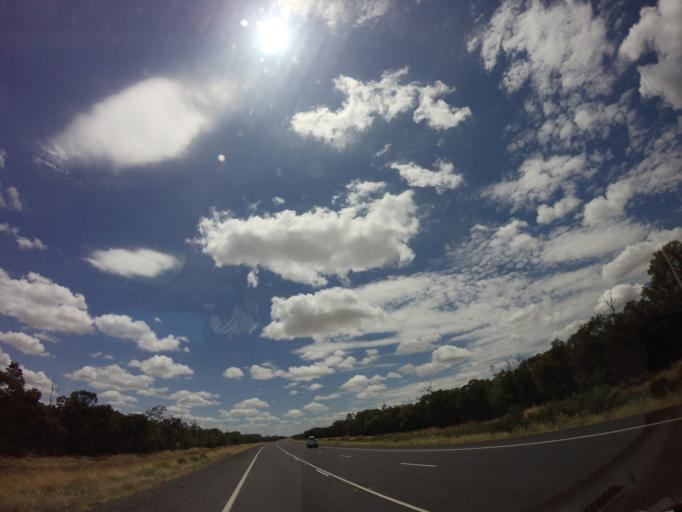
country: AU
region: New South Wales
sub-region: Moree Plains
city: Boggabilla
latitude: -28.8721
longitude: 150.1758
